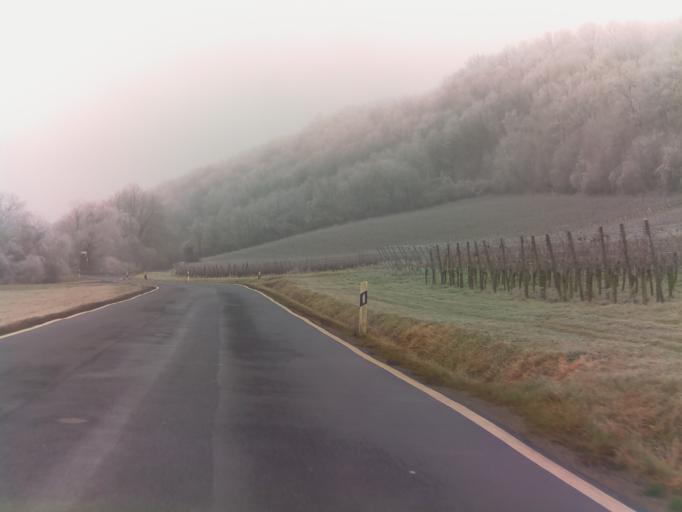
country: DE
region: Bavaria
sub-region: Regierungsbezirk Unterfranken
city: Marktsteft
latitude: 49.6893
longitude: 10.1284
